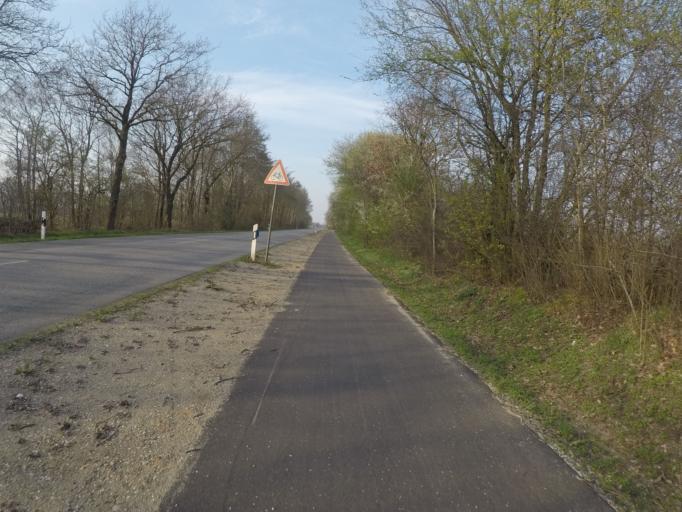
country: DE
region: Schleswig-Holstein
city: Wahlstedt
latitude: 53.9767
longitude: 10.1878
